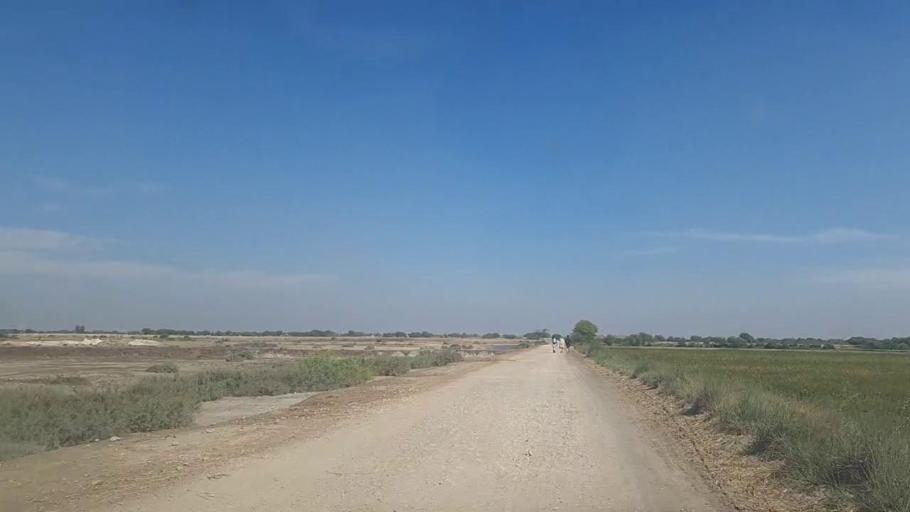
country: PK
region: Sindh
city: Mirpur Batoro
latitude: 24.7049
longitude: 68.2403
